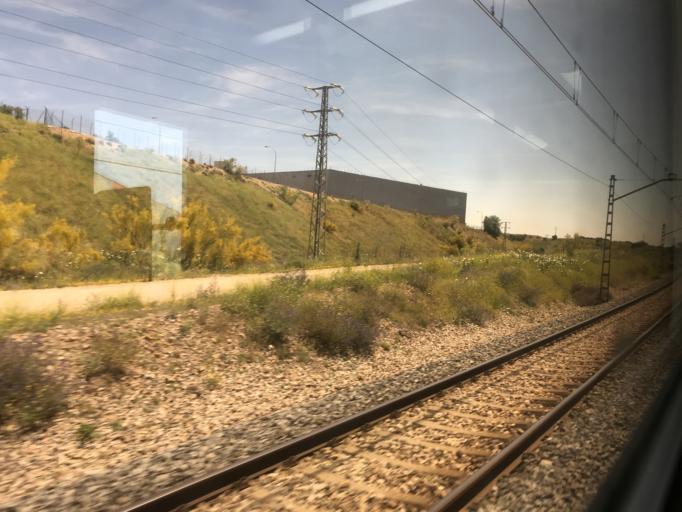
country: ES
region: Madrid
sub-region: Provincia de Madrid
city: Valdemoro
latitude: 40.2119
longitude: -3.6783
